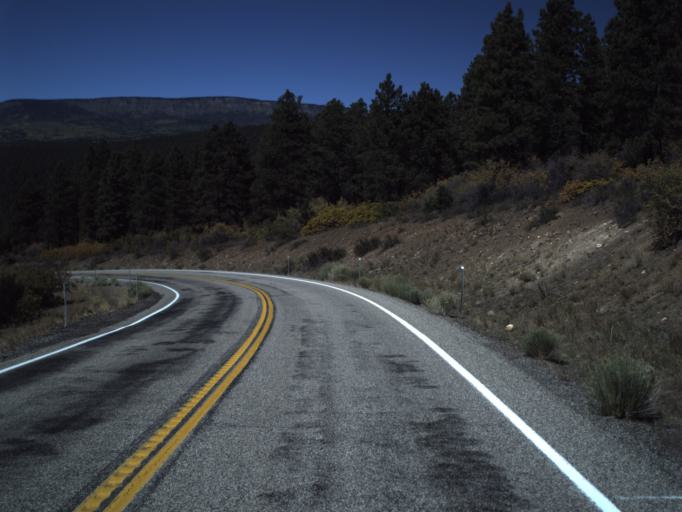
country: US
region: Utah
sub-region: Wayne County
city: Loa
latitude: 37.9919
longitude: -111.4239
